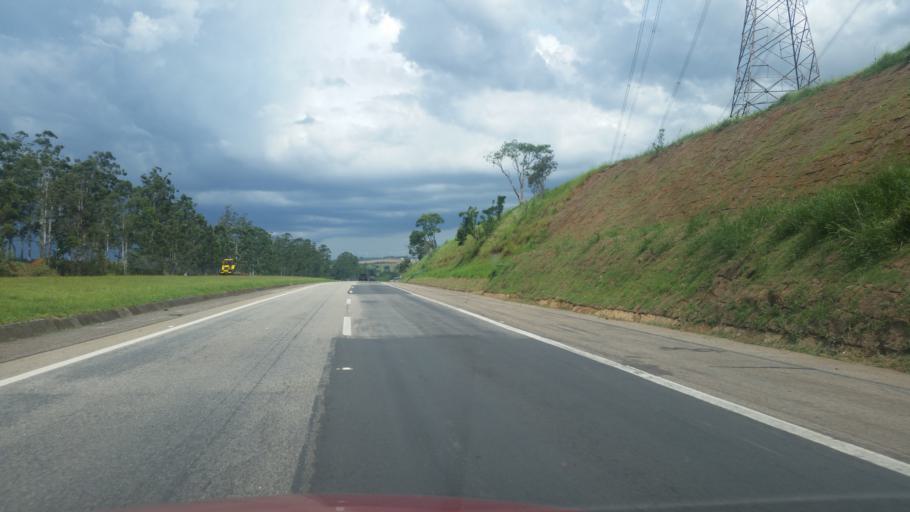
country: BR
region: Sao Paulo
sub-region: Tatui
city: Tatui
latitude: -23.2840
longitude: -47.7824
